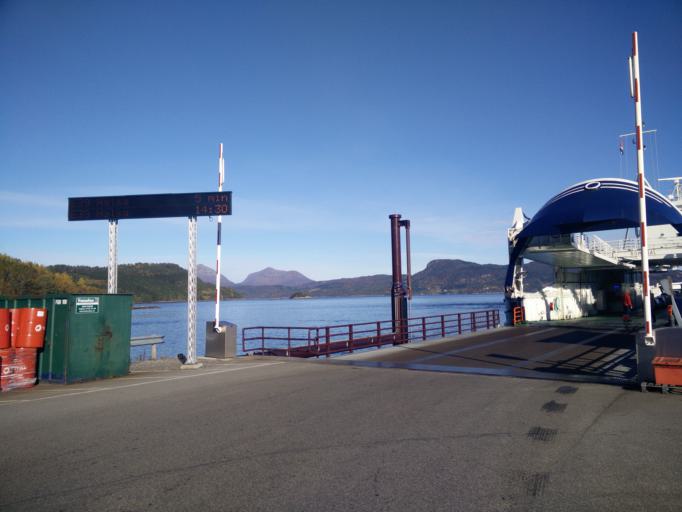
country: NO
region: More og Romsdal
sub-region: Tingvoll
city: Tingvoll
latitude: 63.0532
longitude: 8.1248
